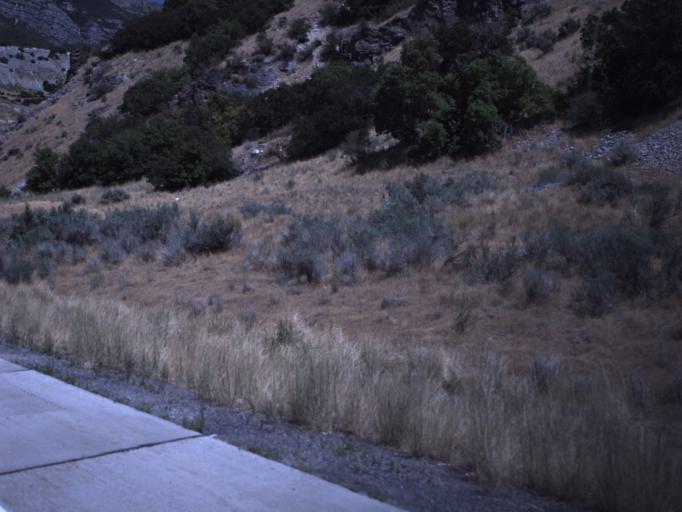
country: US
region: Utah
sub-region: Utah County
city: Orem
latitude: 40.3265
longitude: -111.6417
